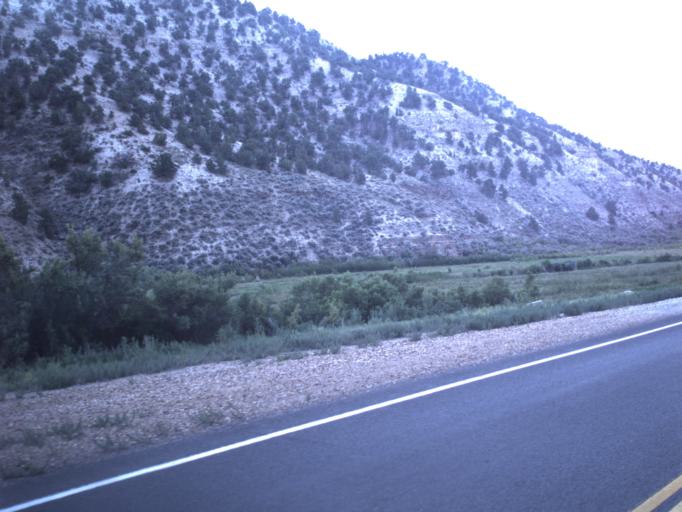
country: US
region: Utah
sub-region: Duchesne County
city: Duchesne
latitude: 40.1047
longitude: -110.4702
